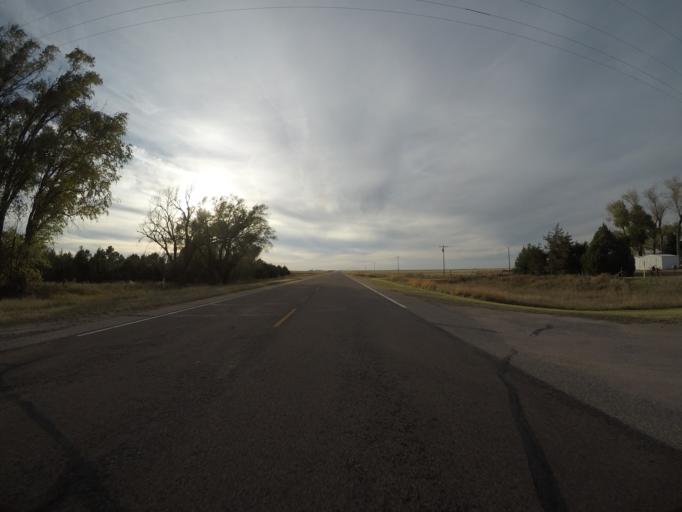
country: US
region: Colorado
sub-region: Kit Carson County
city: Burlington
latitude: 39.6582
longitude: -102.5366
